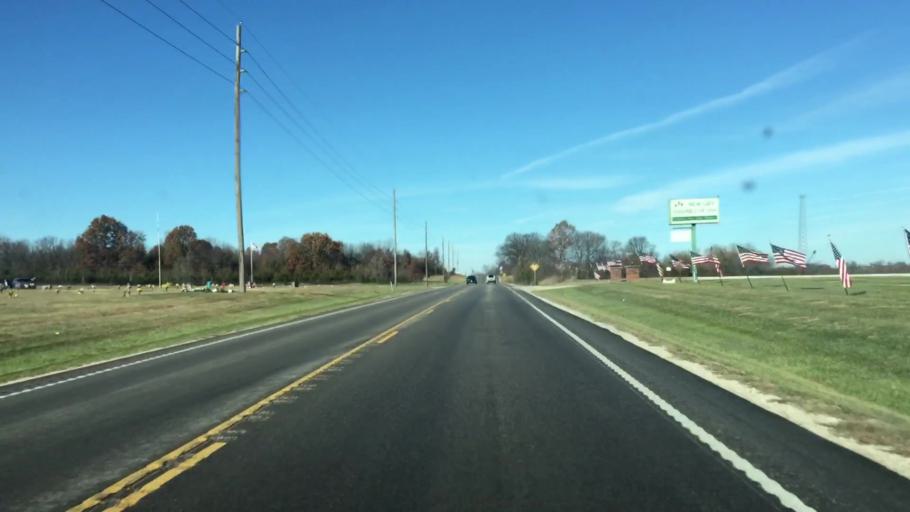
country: US
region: Missouri
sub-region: Miller County
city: Eldon
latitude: 38.3784
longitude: -92.6665
